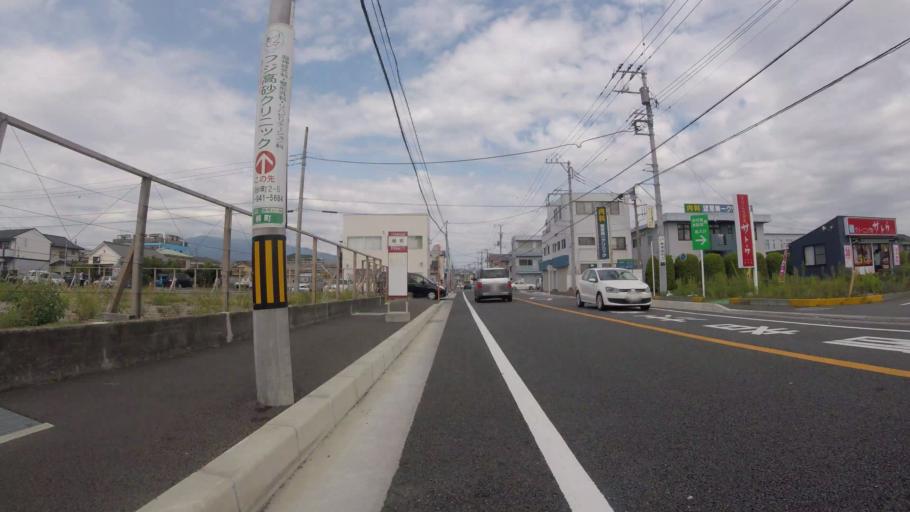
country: JP
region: Shizuoka
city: Numazu
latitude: 35.1167
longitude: 138.8624
